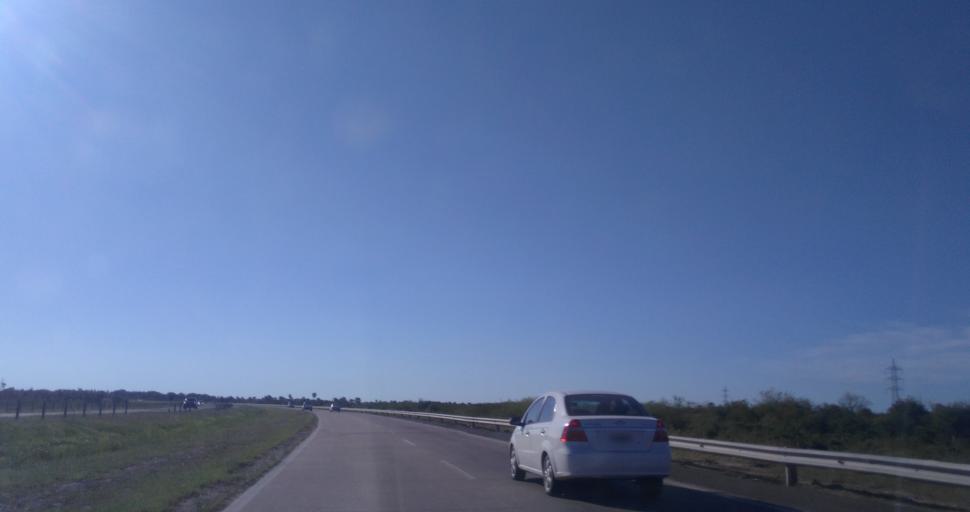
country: AR
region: Chaco
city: Barranqueras
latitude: -27.4382
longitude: -58.8971
